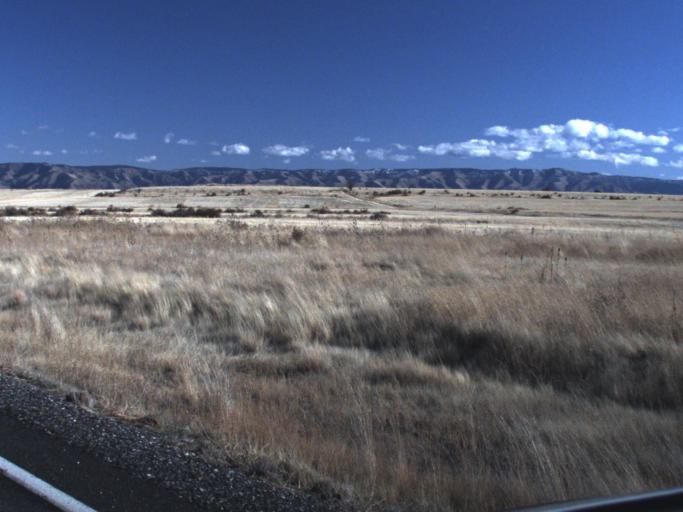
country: US
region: Washington
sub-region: Asotin County
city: Asotin
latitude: 46.1637
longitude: -117.0956
